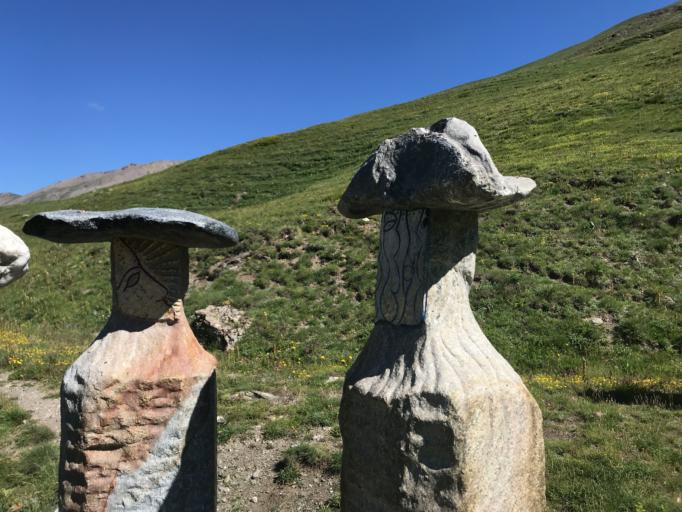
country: IT
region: Piedmont
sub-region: Provincia di Cuneo
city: Pontechianale
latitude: 44.7079
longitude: 6.9304
